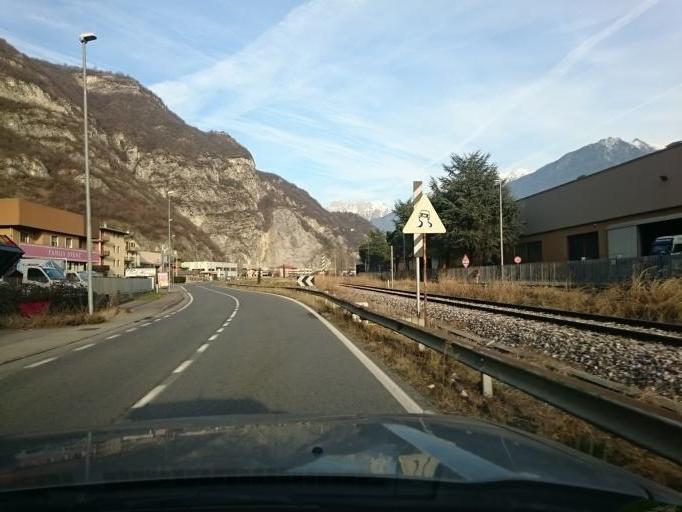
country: IT
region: Lombardy
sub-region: Provincia di Brescia
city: Cividate Camuno
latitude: 45.9398
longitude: 10.2560
